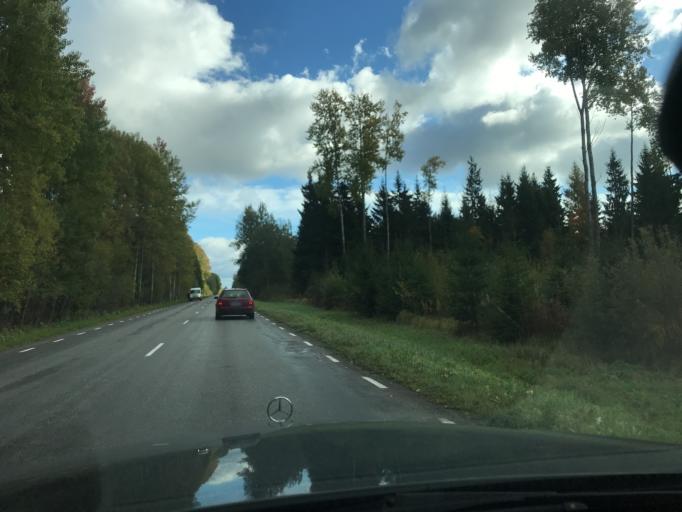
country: EE
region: Vorumaa
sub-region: Antsla vald
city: Vana-Antsla
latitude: 57.9047
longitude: 26.4411
